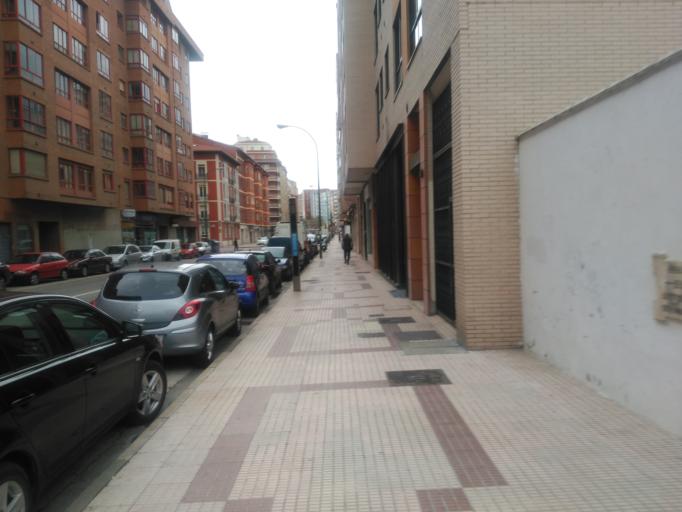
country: ES
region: Castille and Leon
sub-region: Provincia de Burgos
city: Burgos
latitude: 42.3308
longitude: -3.7001
